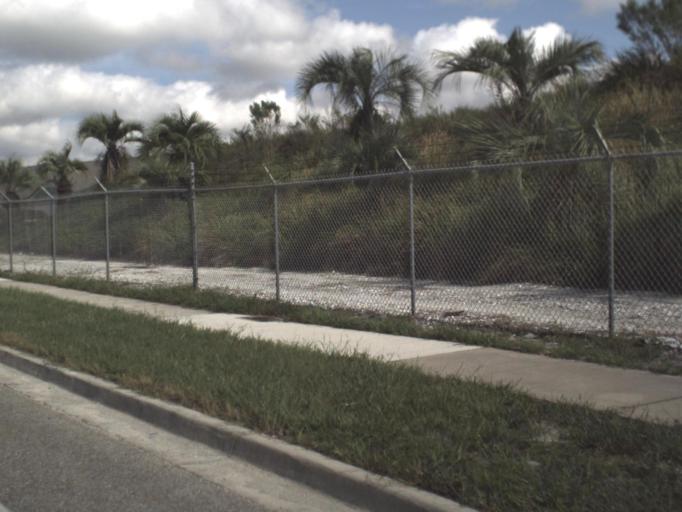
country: US
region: Florida
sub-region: Manatee County
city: Whitfield
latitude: 27.4024
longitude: -82.5662
